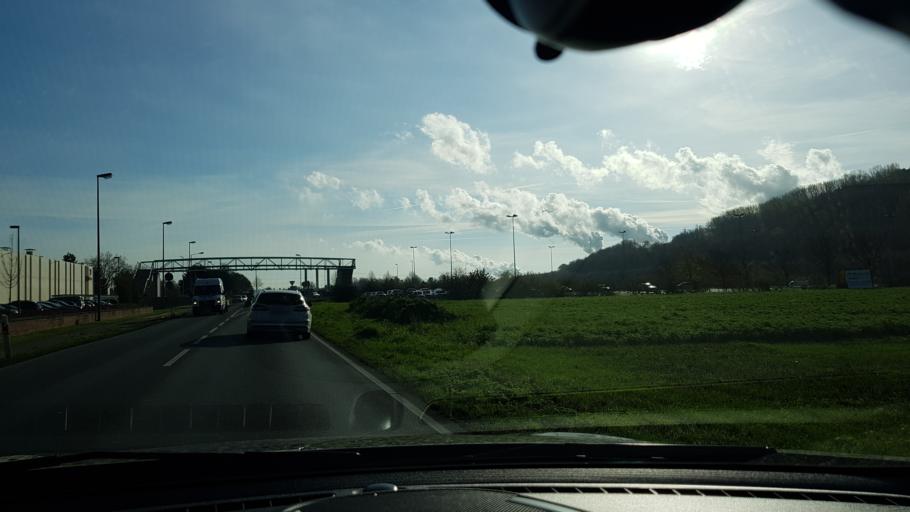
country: DE
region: North Rhine-Westphalia
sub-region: Regierungsbezirk Dusseldorf
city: Grevenbroich
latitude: 51.0766
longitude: 6.6195
